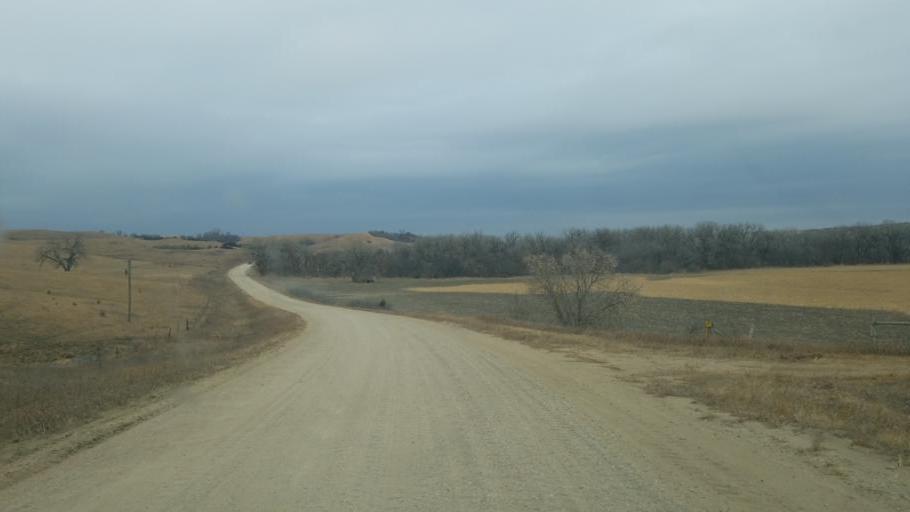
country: US
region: Nebraska
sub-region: Knox County
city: Center
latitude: 42.6837
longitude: -97.8974
